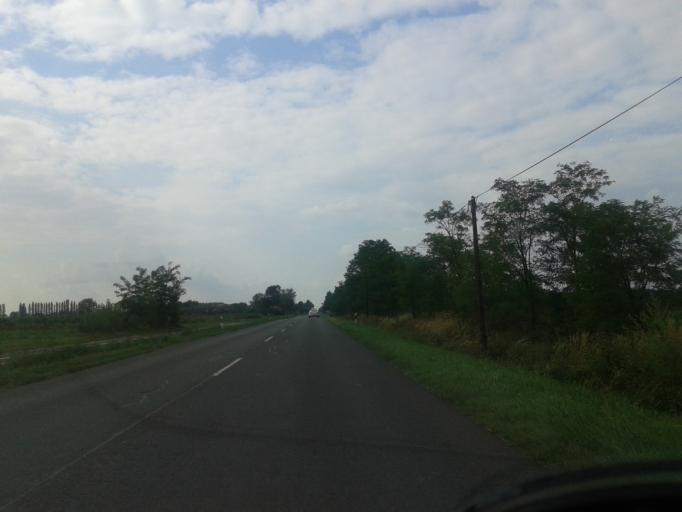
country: HU
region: Bacs-Kiskun
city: Akaszto
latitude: 46.6732
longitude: 19.2230
